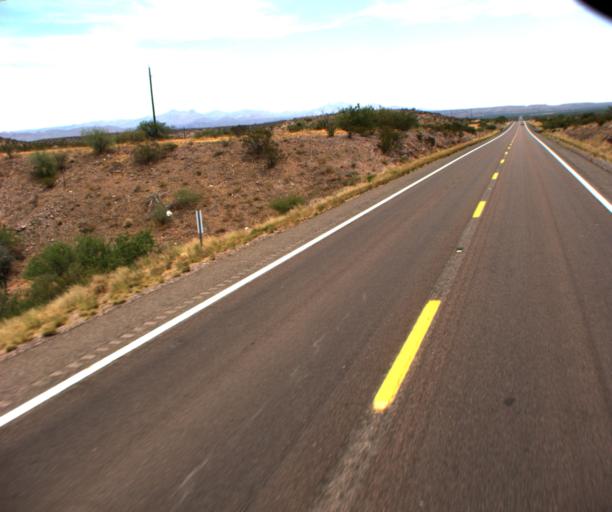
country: US
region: Arizona
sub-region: Graham County
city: Bylas
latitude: 33.2004
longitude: -110.1880
